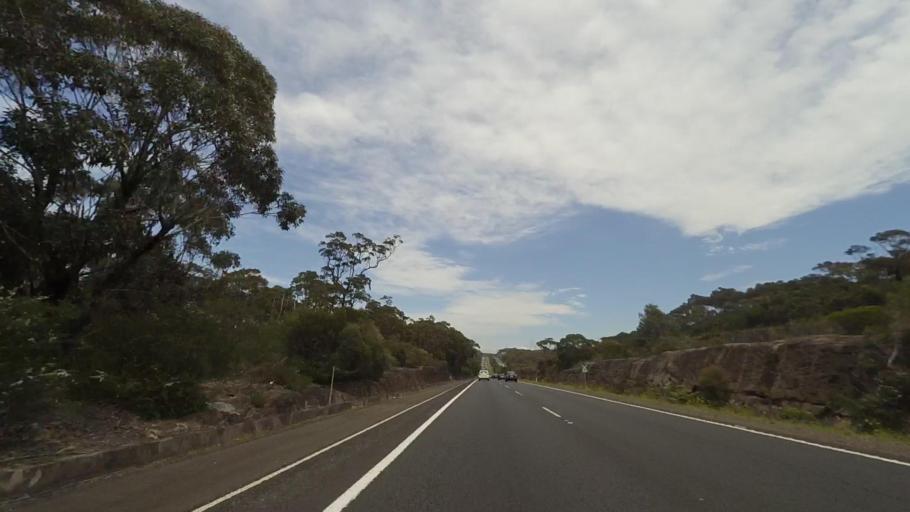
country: AU
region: New South Wales
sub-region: Wollongong
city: Helensburgh
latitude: -34.2131
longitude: 150.9591
